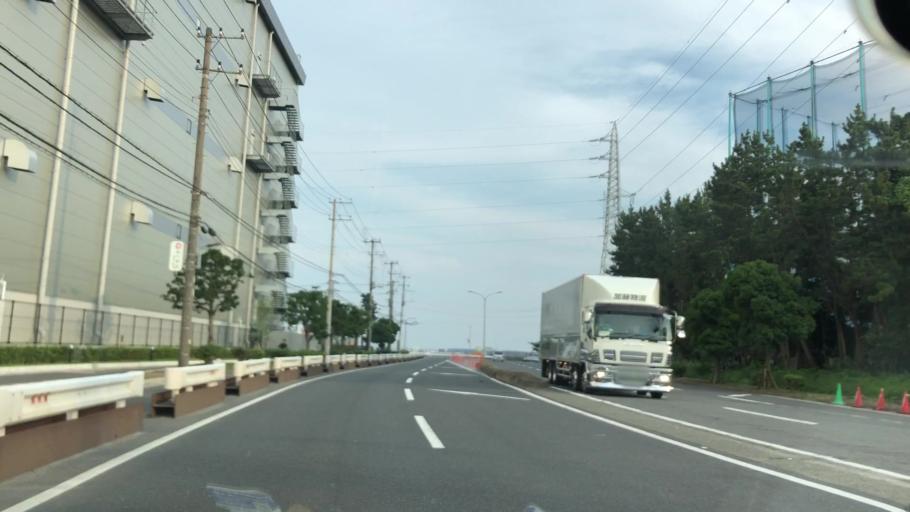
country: JP
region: Tokyo
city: Urayasu
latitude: 35.6681
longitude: 139.9301
